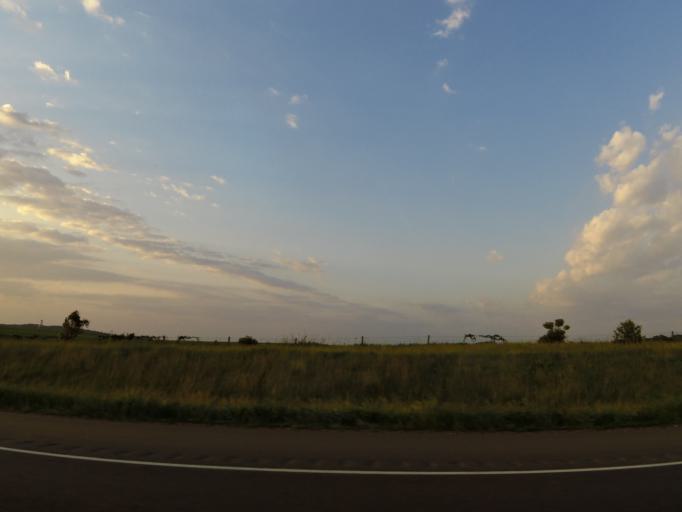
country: US
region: Wisconsin
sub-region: Dunn County
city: Colfax
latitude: 44.8597
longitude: -91.6675
